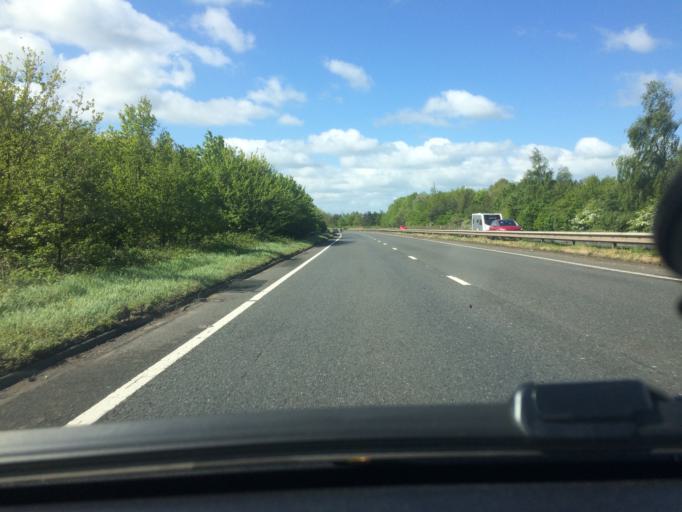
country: GB
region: England
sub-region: Cheshire West and Chester
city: Hoole
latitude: 53.1810
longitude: -2.8512
